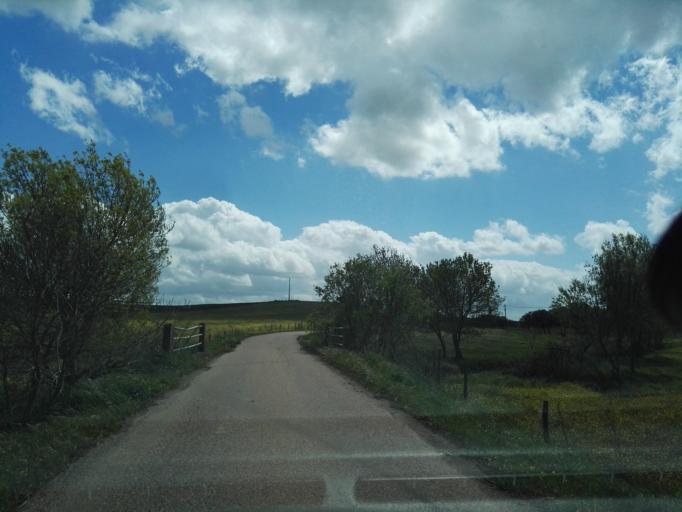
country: PT
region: Portalegre
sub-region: Elvas
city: Elvas
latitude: 38.9716
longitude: -7.1729
